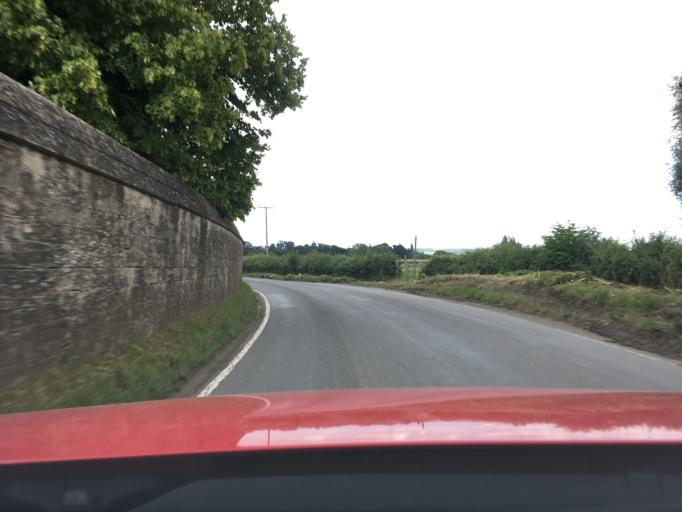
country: GB
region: England
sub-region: Gloucestershire
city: Dursley
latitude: 51.7800
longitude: -2.3862
